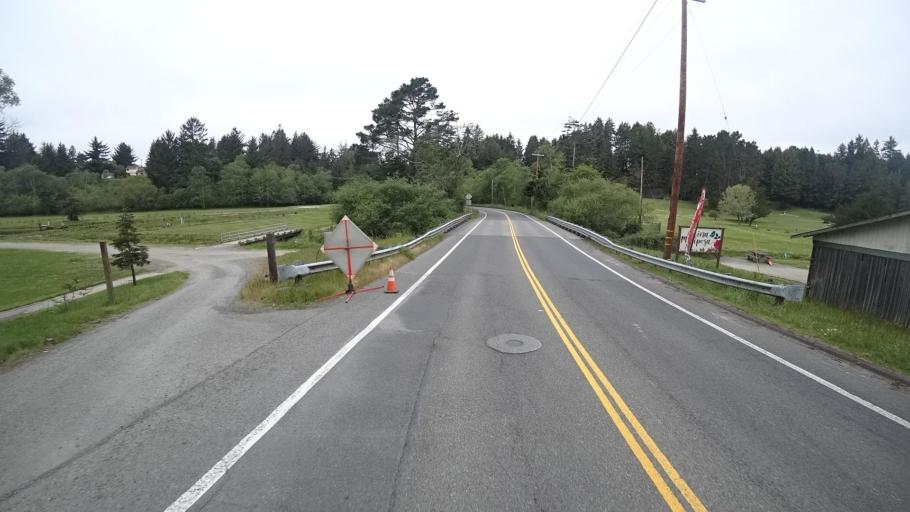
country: US
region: California
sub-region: Humboldt County
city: Bayview
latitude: 40.7583
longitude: -124.1702
